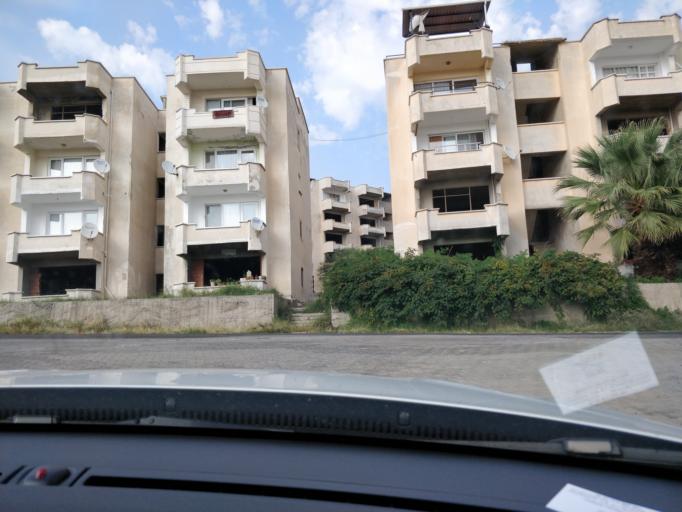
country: TR
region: Balikesir
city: Ayvalik
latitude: 39.2735
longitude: 26.6502
